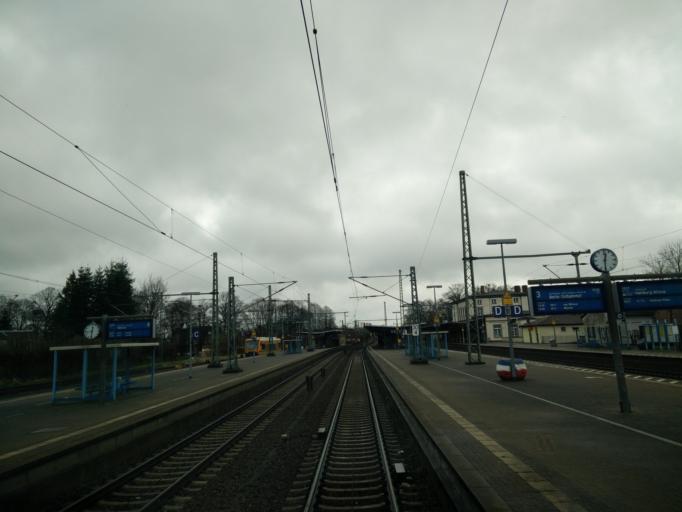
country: DE
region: Mecklenburg-Vorpommern
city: Ludwigslust
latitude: 53.3356
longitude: 11.4931
